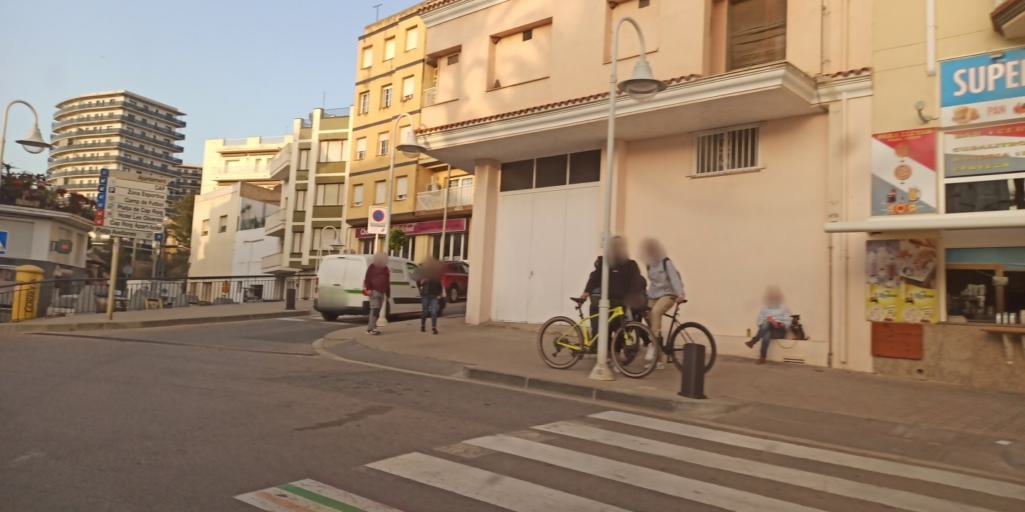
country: ES
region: Catalonia
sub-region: Provincia de Tarragona
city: L'Ampolla
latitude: 40.8124
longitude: 0.7114
